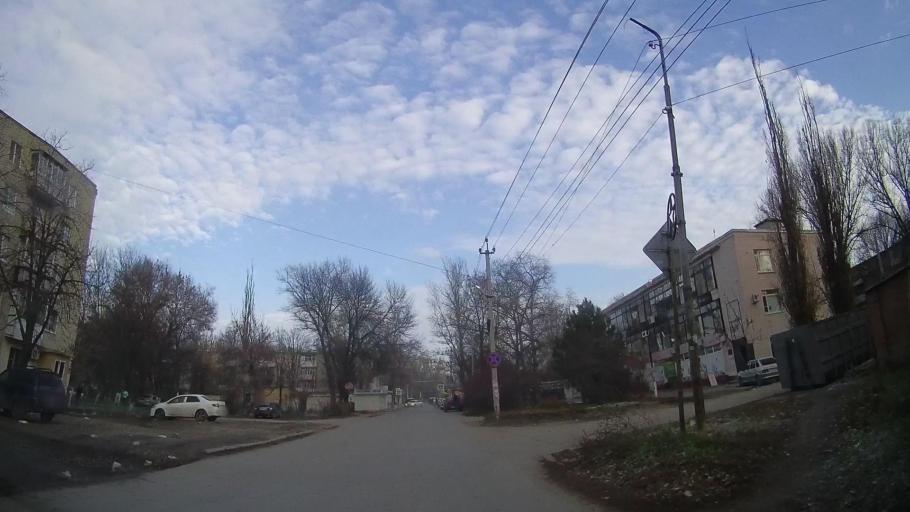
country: RU
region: Rostov
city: Bataysk
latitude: 47.1258
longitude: 39.7788
